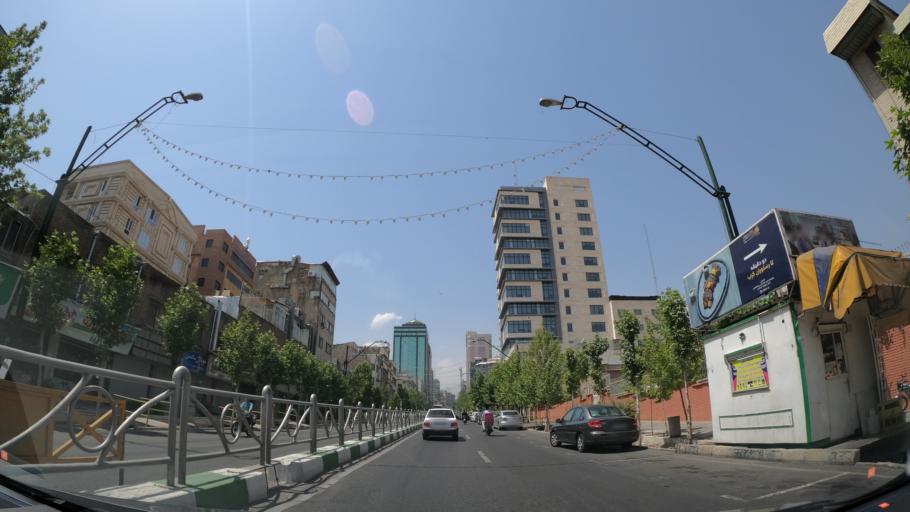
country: IR
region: Tehran
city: Tehran
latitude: 35.7295
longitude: 51.4125
